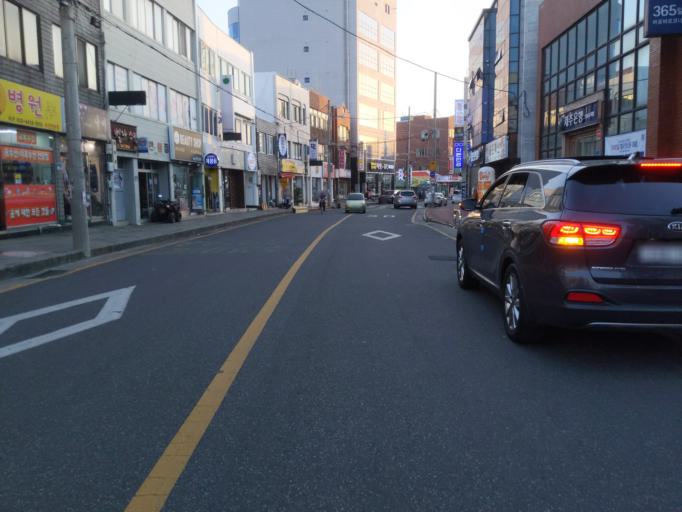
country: KR
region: Jeju-do
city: Gaigeturi
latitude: 33.2218
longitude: 126.2537
